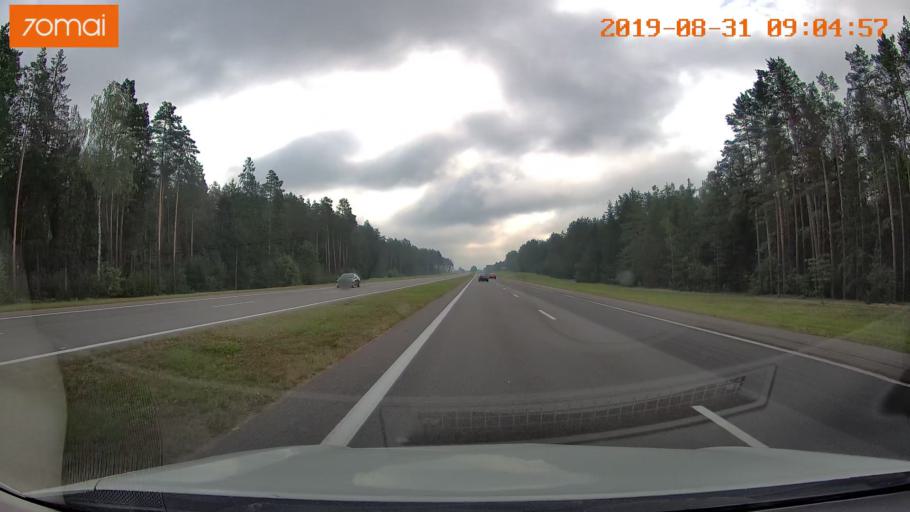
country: BY
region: Minsk
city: Chervyen'
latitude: 53.7290
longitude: 28.3612
